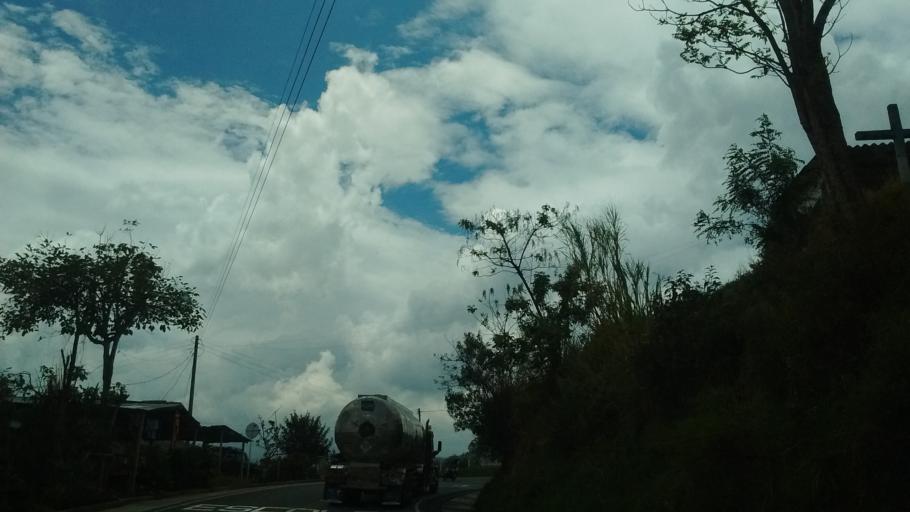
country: CO
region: Cauca
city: Rosas
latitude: 2.3274
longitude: -76.6928
